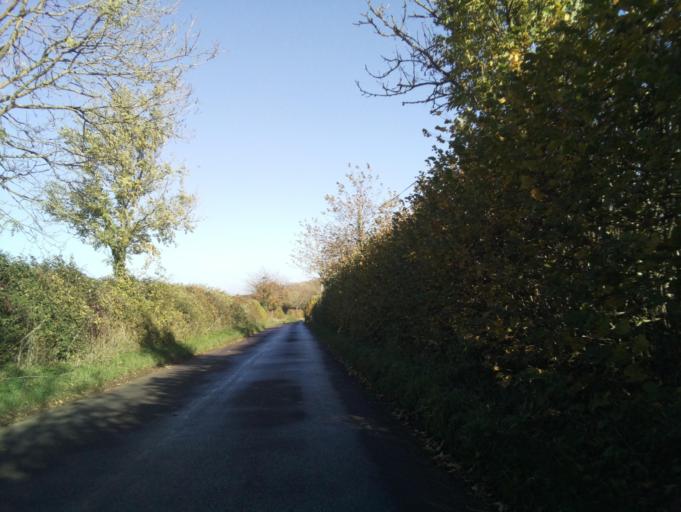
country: GB
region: England
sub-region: Somerset
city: Bruton
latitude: 51.0855
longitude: -2.4642
